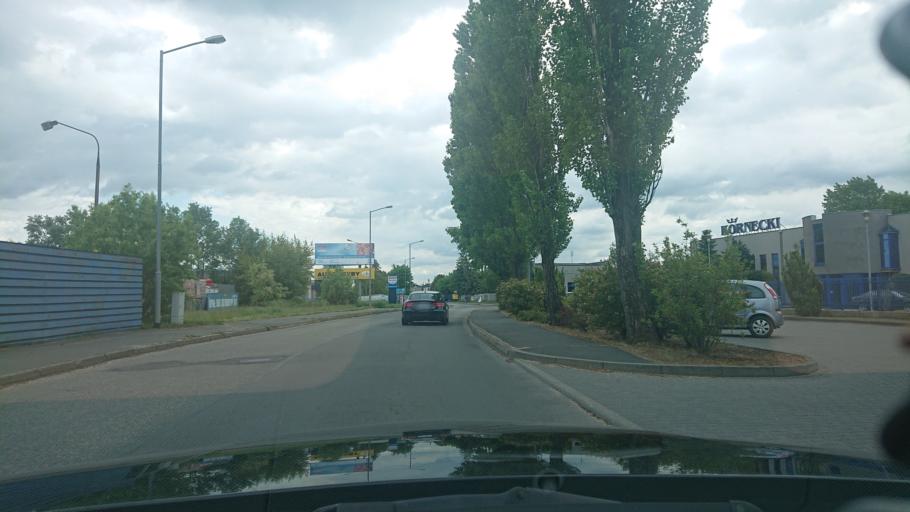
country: PL
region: Greater Poland Voivodeship
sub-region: Powiat gnieznienski
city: Gniezno
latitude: 52.5395
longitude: 17.6292
